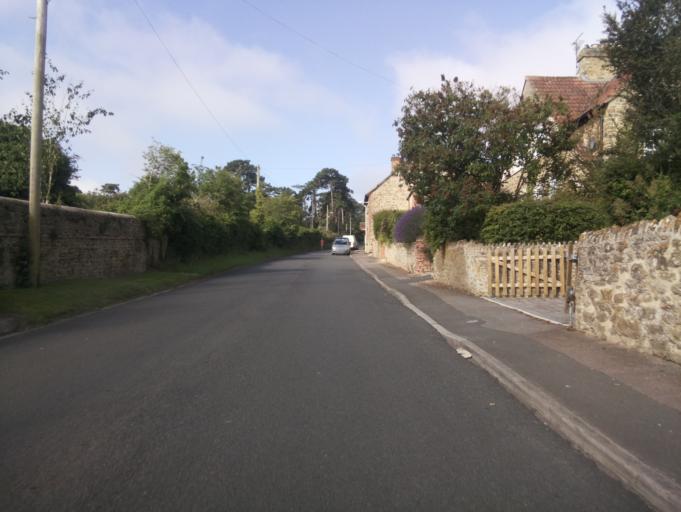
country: GB
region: England
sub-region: Borough of Swindon
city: Highworth
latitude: 51.6301
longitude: -1.7022
